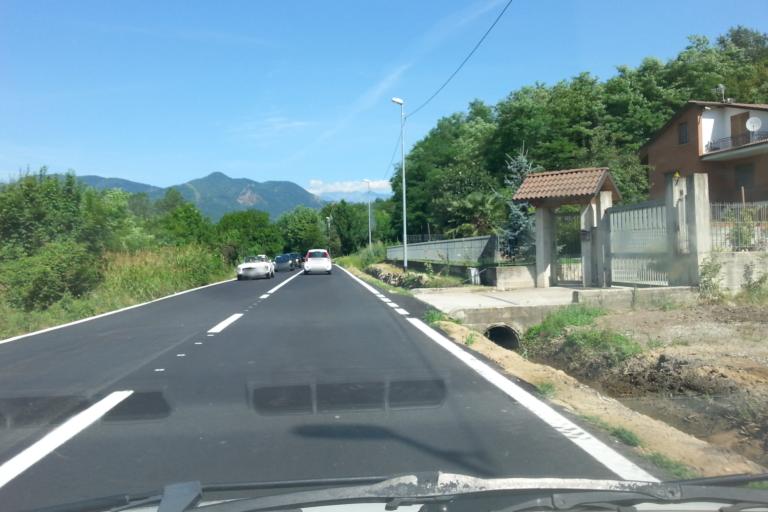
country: IT
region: Piedmont
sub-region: Provincia di Torino
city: Trana
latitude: 45.0486
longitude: 7.4043
